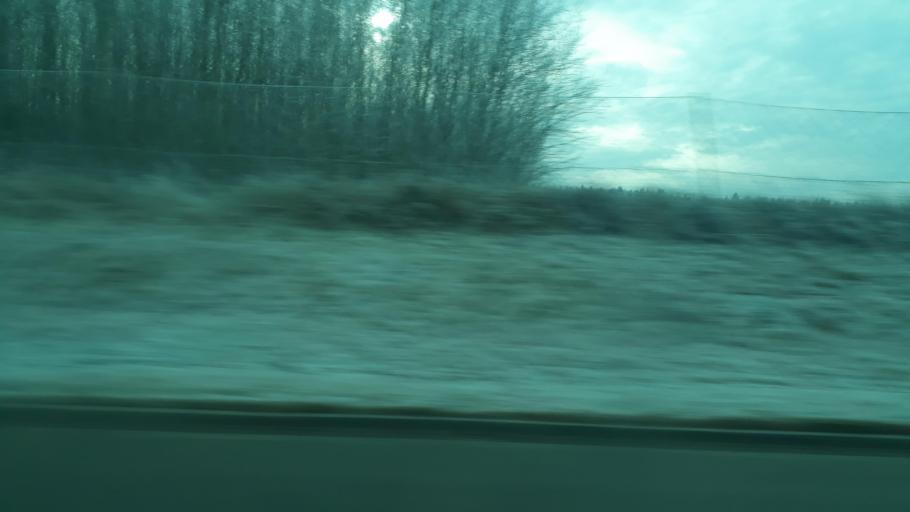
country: CZ
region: Plzensky
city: Hermanova Hut'
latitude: 49.7132
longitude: 13.1543
